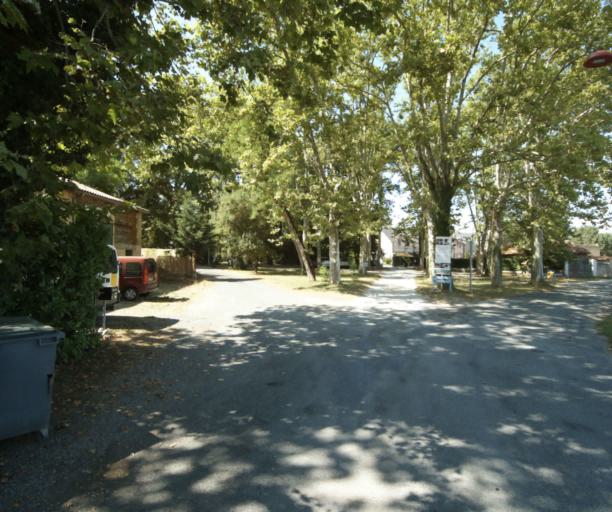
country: FR
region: Midi-Pyrenees
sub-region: Departement de la Haute-Garonne
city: Revel
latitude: 43.4963
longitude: 1.9693
